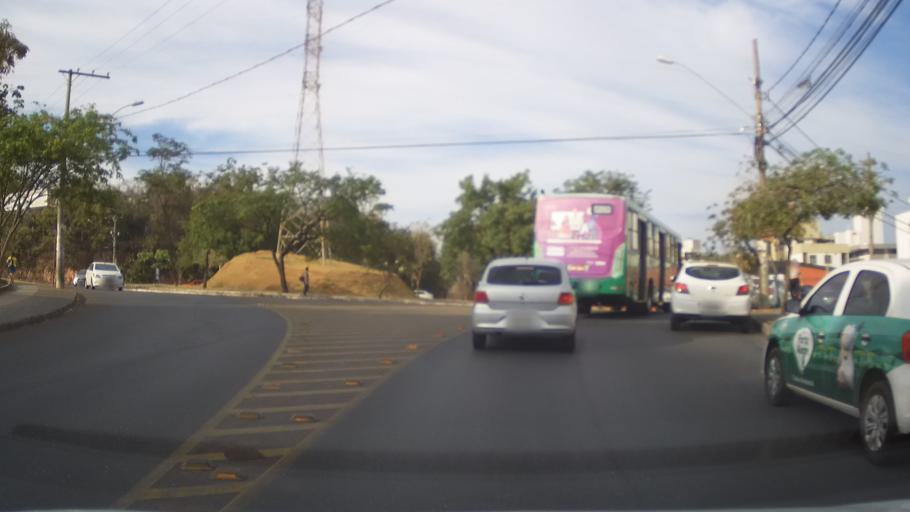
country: BR
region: Minas Gerais
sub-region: Belo Horizonte
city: Belo Horizonte
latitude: -19.8816
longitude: -43.9992
